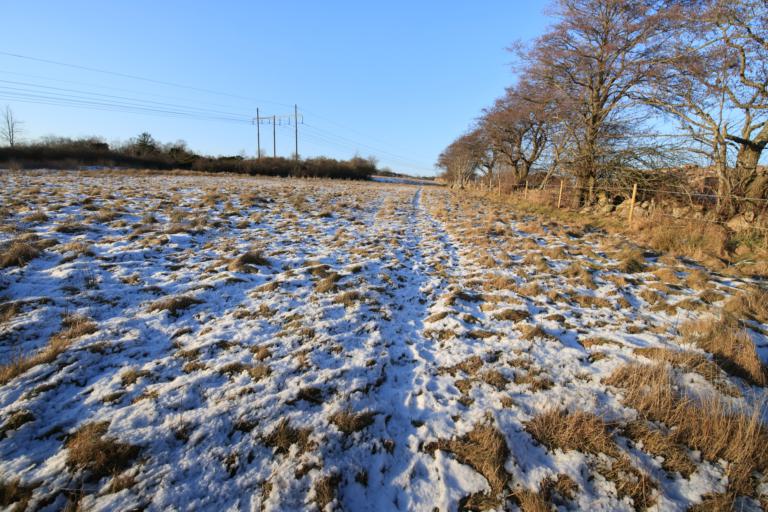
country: SE
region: Halland
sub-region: Varbergs Kommun
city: Varberg
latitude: 57.1293
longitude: 12.3029
